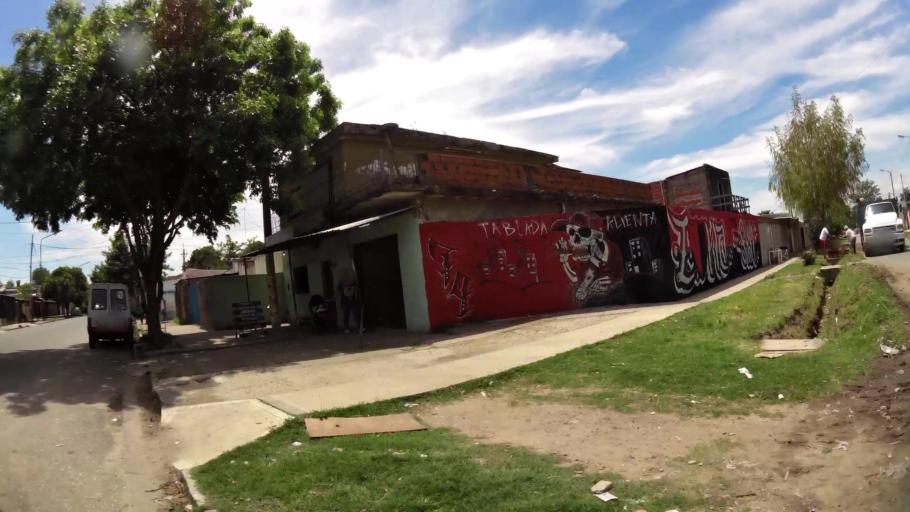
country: AR
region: Santa Fe
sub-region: Departamento de Rosario
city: Rosario
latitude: -32.9869
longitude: -60.6363
